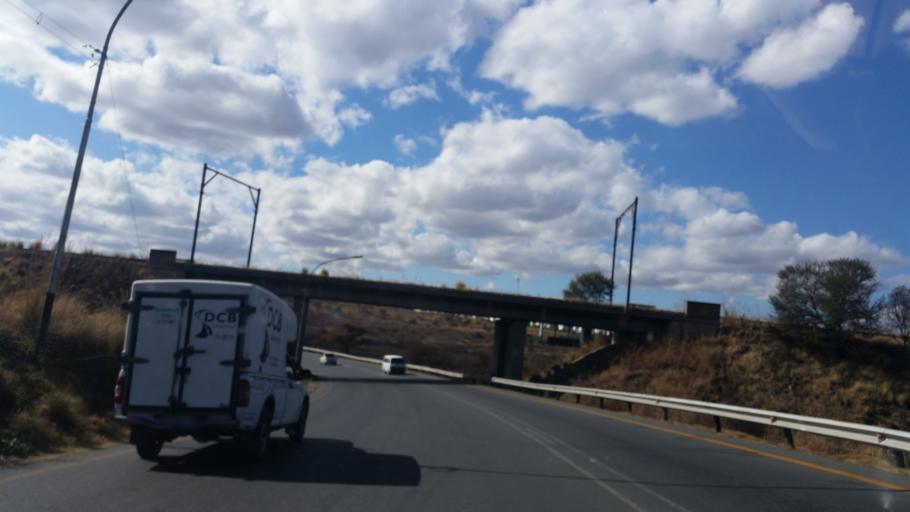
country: ZA
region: KwaZulu-Natal
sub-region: uThukela District Municipality
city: Ladysmith
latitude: -28.5492
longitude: 29.7928
